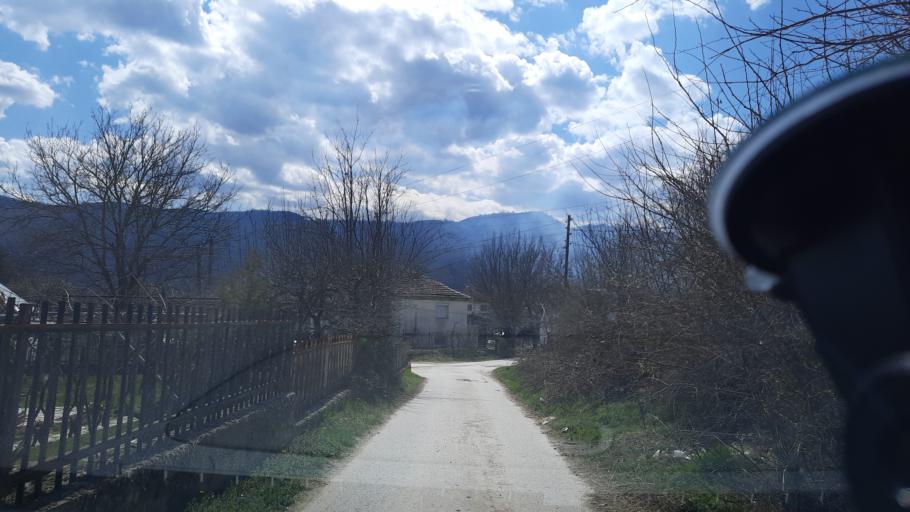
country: MK
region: Demir Hisar
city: Sopotnica
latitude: 41.2947
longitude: 21.1515
